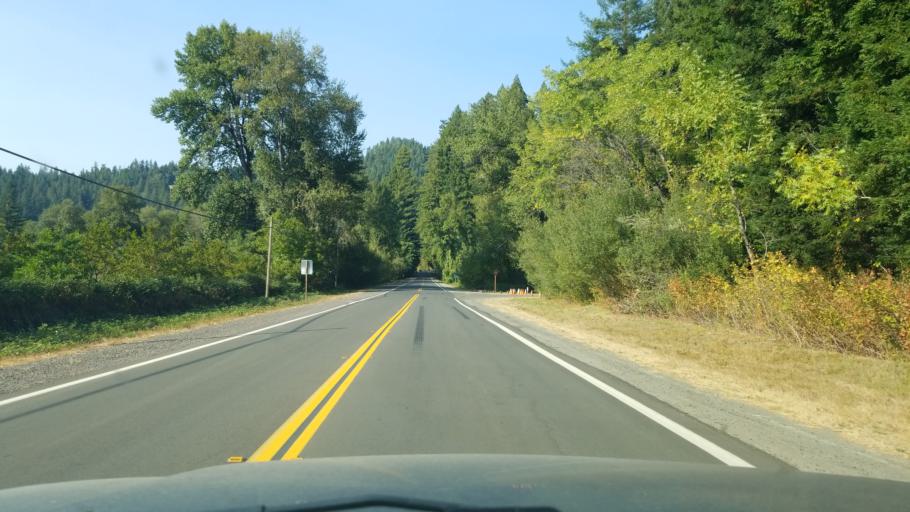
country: US
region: California
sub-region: Humboldt County
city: Redway
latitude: 40.2140
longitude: -123.7867
